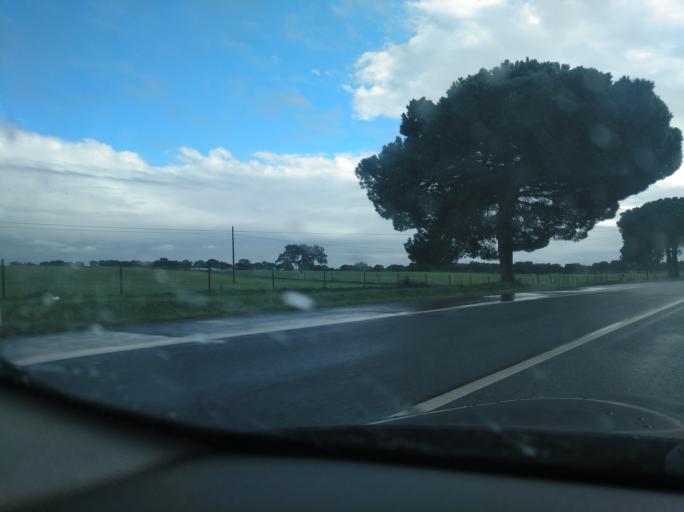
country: PT
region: Beja
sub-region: Aljustrel
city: Aljustrel
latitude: 38.0059
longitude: -8.3775
